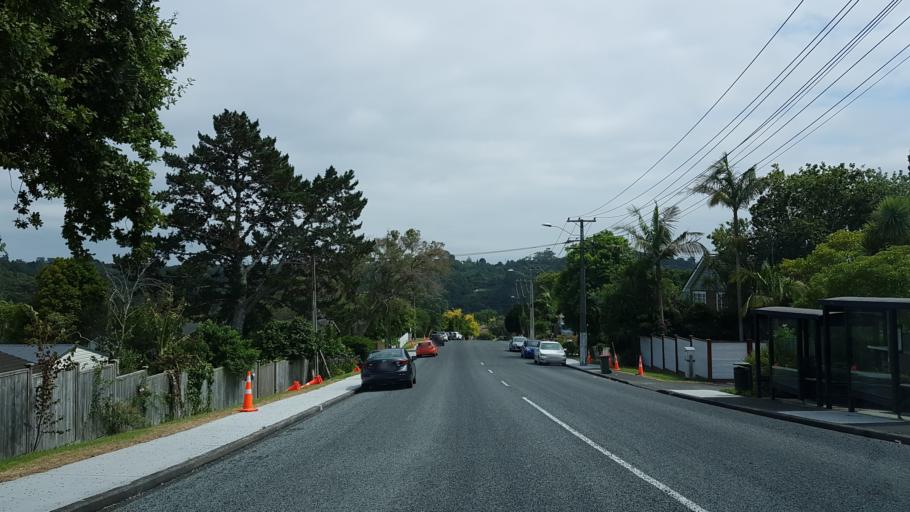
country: NZ
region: Auckland
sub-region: Auckland
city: North Shore
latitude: -36.7795
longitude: 174.7050
